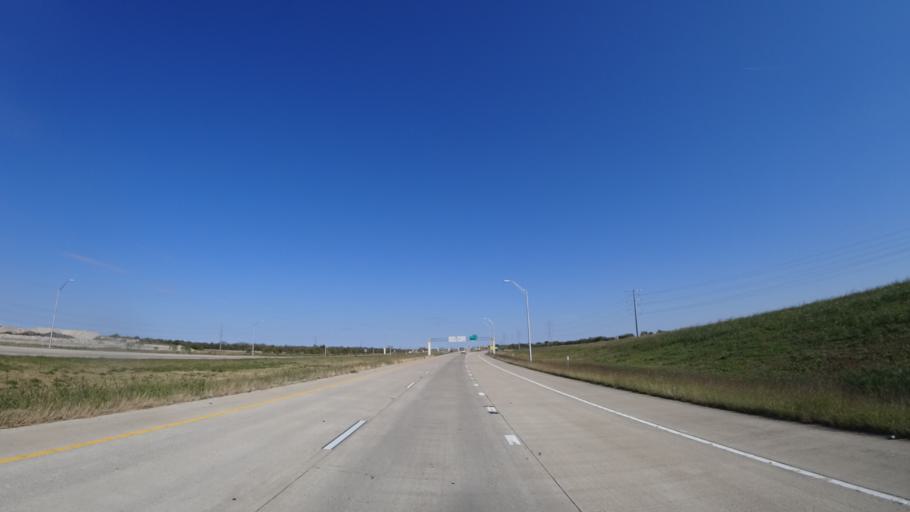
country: US
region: Texas
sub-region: Travis County
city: Garfield
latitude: 30.1648
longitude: -97.6506
